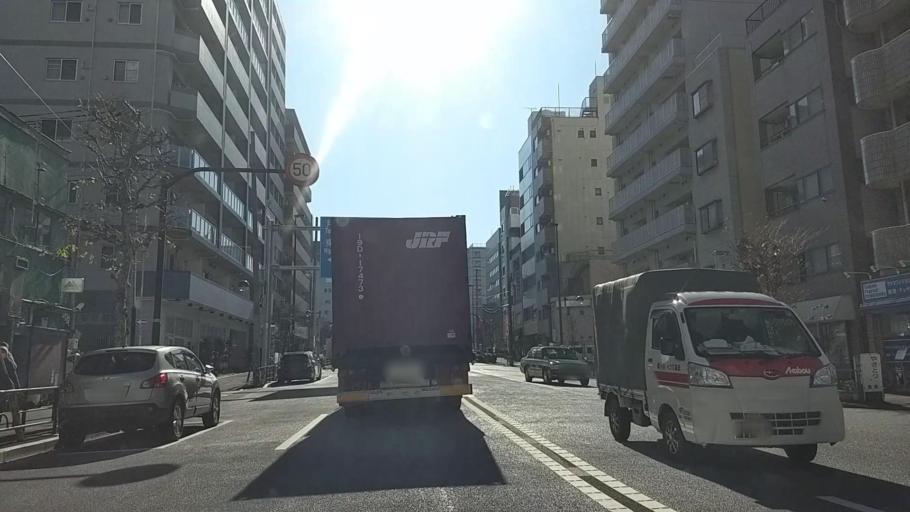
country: JP
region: Tokyo
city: Urayasu
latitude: 35.6849
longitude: 139.7985
